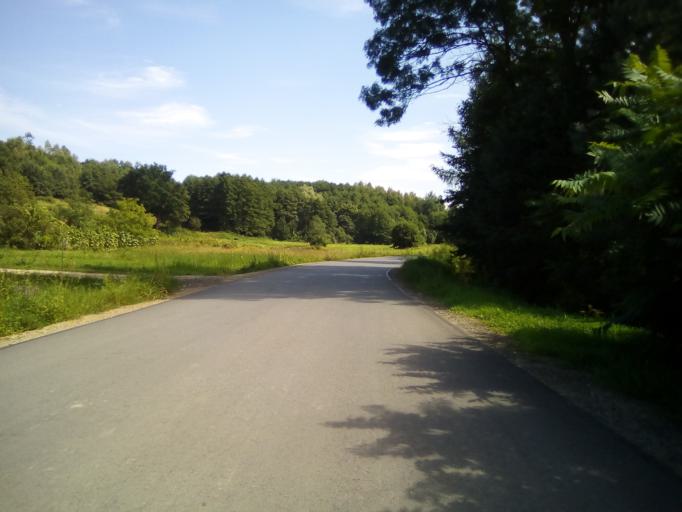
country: PL
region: Subcarpathian Voivodeship
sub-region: Powiat brzozowski
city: Domaradz
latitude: 49.8086
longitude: 21.9281
